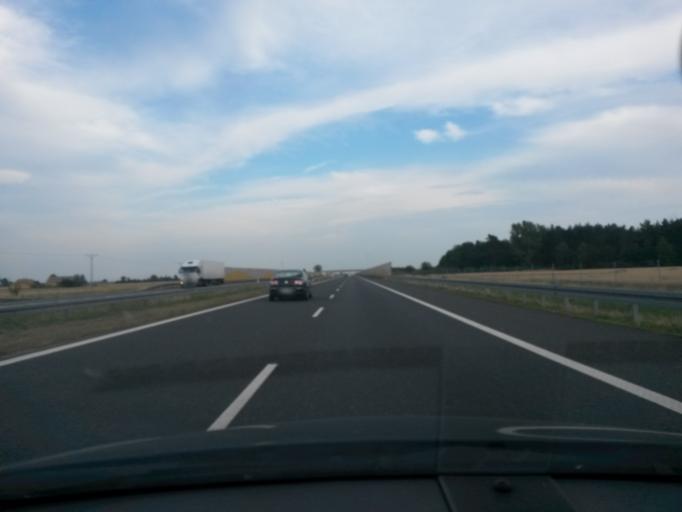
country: PL
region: Lodz Voivodeship
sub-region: Powiat leczycki
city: Swinice Warckie
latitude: 52.0222
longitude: 18.9275
